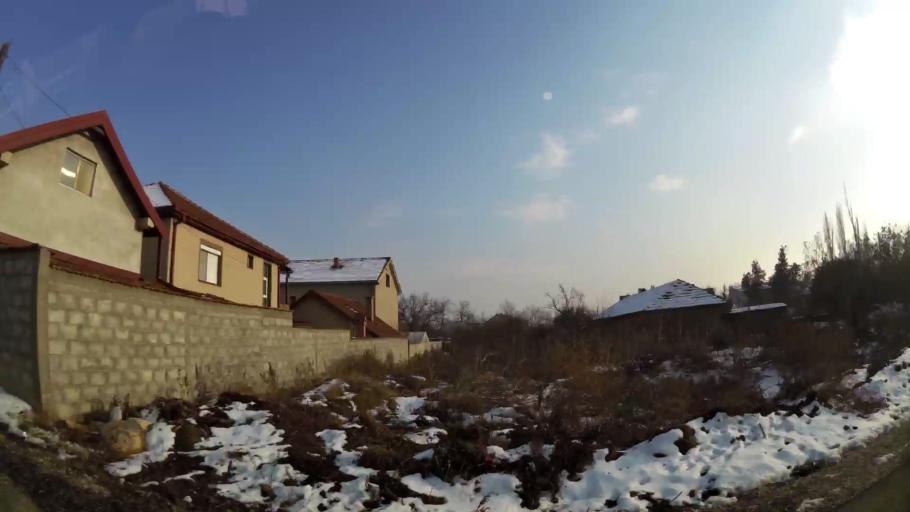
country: MK
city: Creshevo
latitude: 42.0269
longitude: 21.5108
